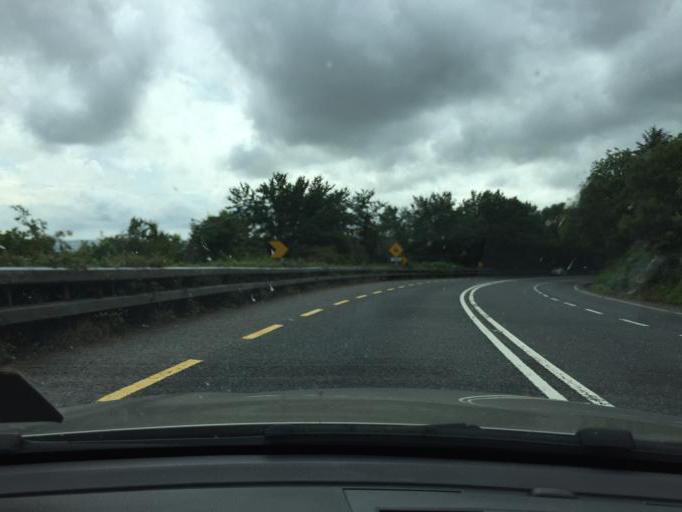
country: IE
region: Munster
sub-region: Waterford
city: Dungarvan
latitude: 52.1145
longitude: -7.5581
